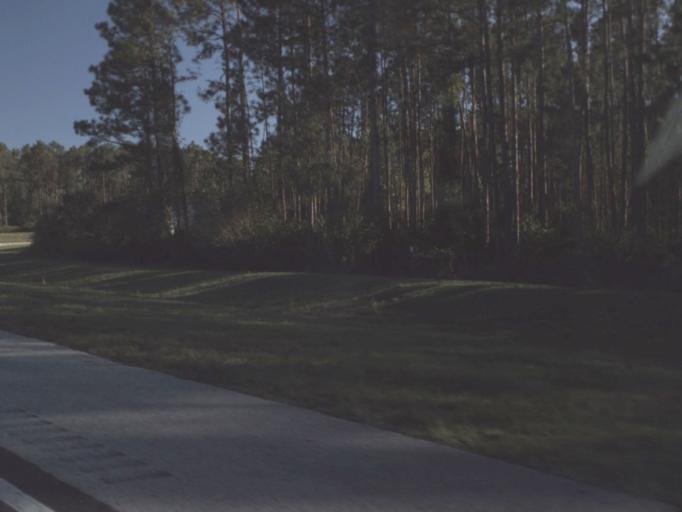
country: US
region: Florida
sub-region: Flagler County
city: Palm Coast
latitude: 29.6442
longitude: -81.2725
